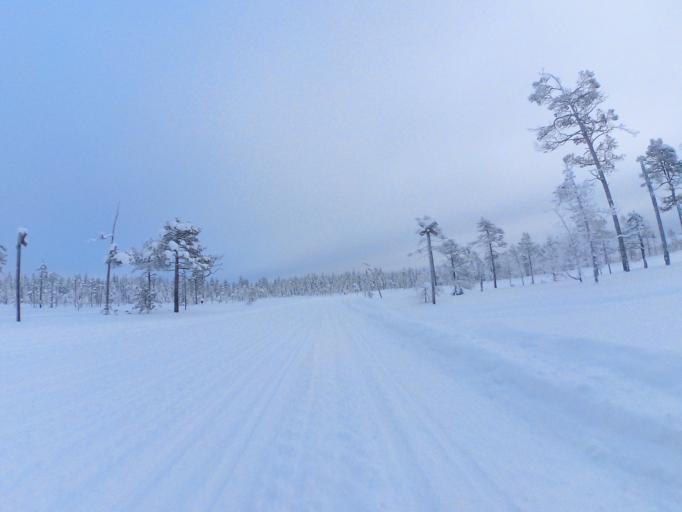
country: FI
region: Lapland
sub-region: Rovaniemi
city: Rovaniemi
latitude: 66.6292
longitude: 26.0223
